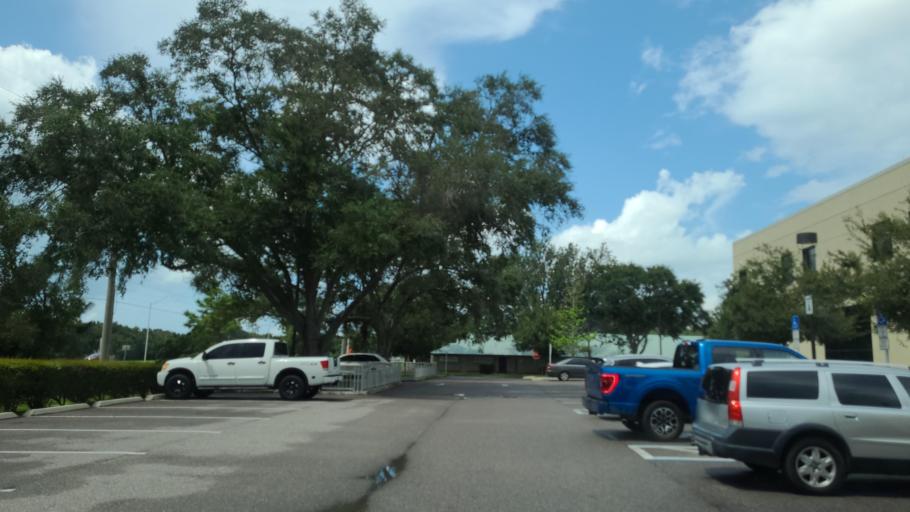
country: US
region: Florida
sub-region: Hillsborough County
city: Sun City Center
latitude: 27.7128
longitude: -82.3653
